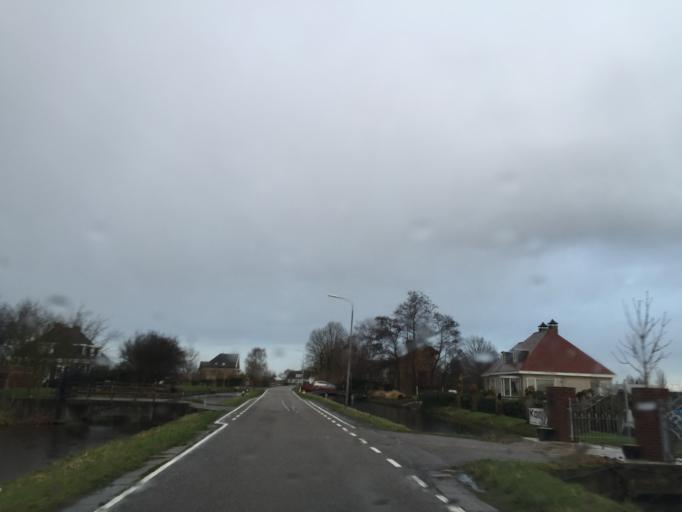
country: NL
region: South Holland
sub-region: Gemeente Pijnacker-Nootdorp
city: Pijnacker
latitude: 51.9898
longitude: 4.4304
